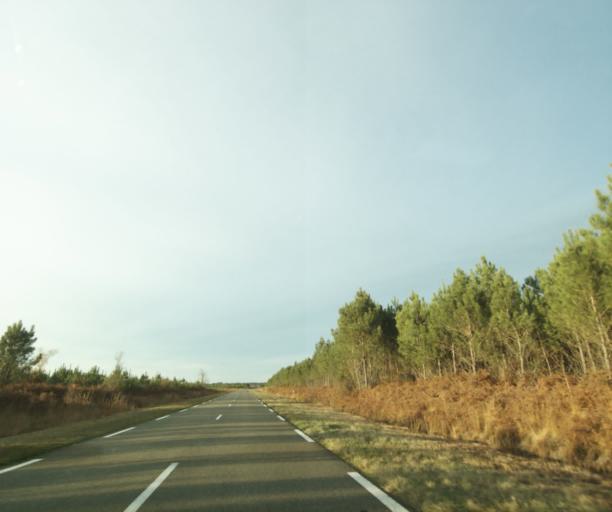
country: FR
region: Aquitaine
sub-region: Departement des Landes
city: Gabarret
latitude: 44.0771
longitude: -0.0684
